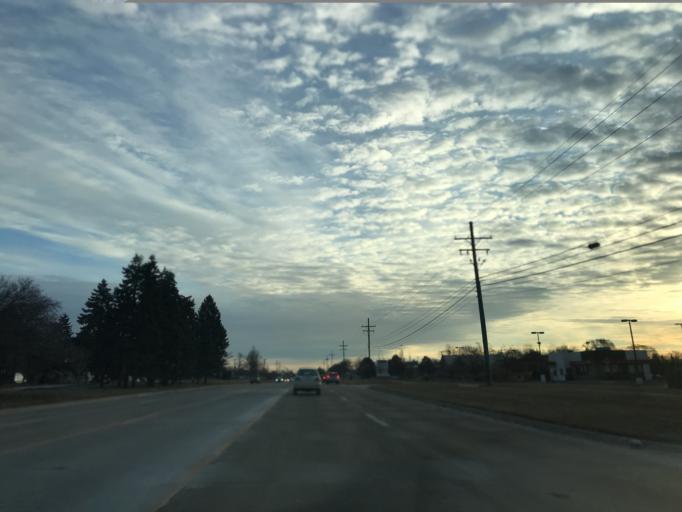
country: US
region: Michigan
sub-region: Oakland County
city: Farmington
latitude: 42.4404
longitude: -83.3817
